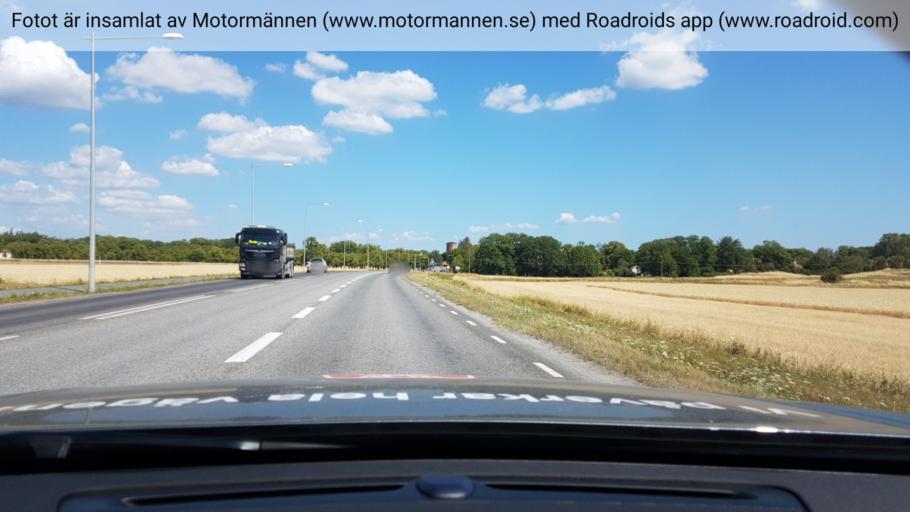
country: SE
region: Stockholm
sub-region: Ekero Kommun
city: Ekeroe
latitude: 59.3162
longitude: 17.8630
